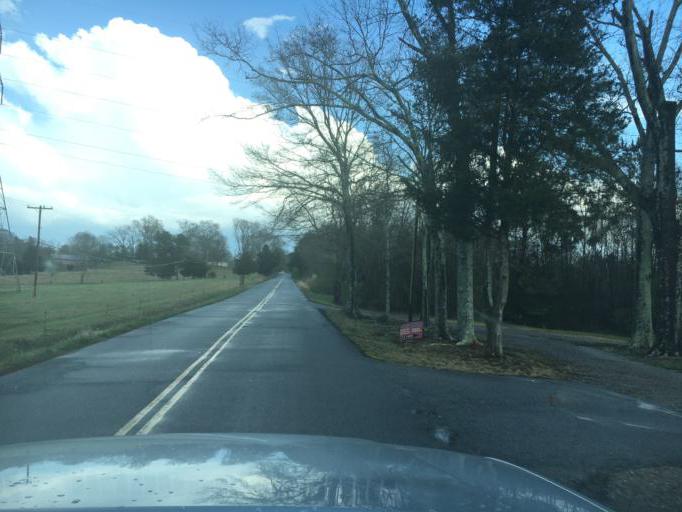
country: US
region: South Carolina
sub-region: Greenville County
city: Berea
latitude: 34.8644
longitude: -82.5086
